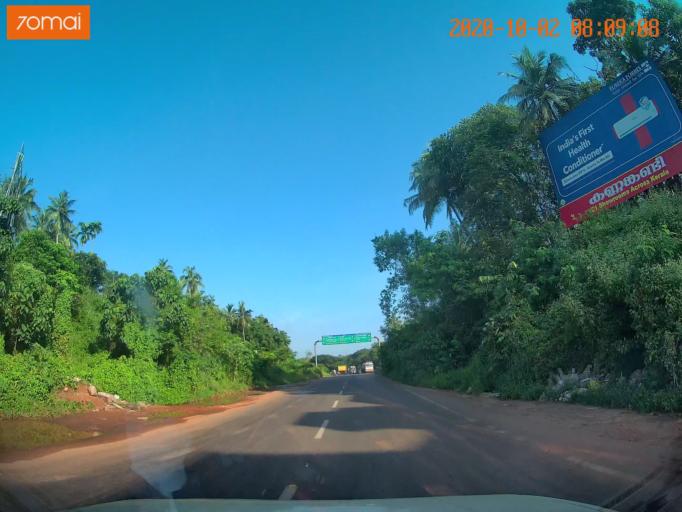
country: IN
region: Kerala
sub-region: Kozhikode
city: Kozhikode
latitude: 11.2601
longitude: 75.8214
